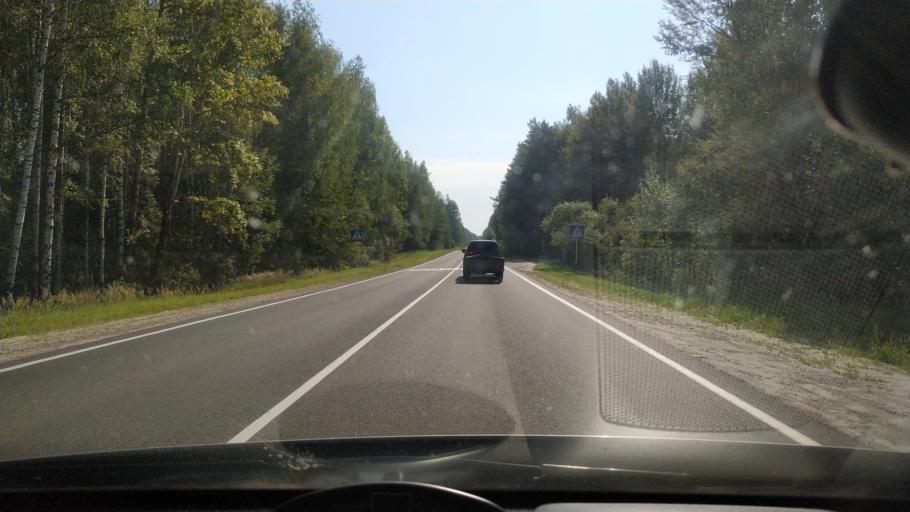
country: RU
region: Rjazan
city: Spas-Klepiki
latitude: 55.2239
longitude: 40.0716
